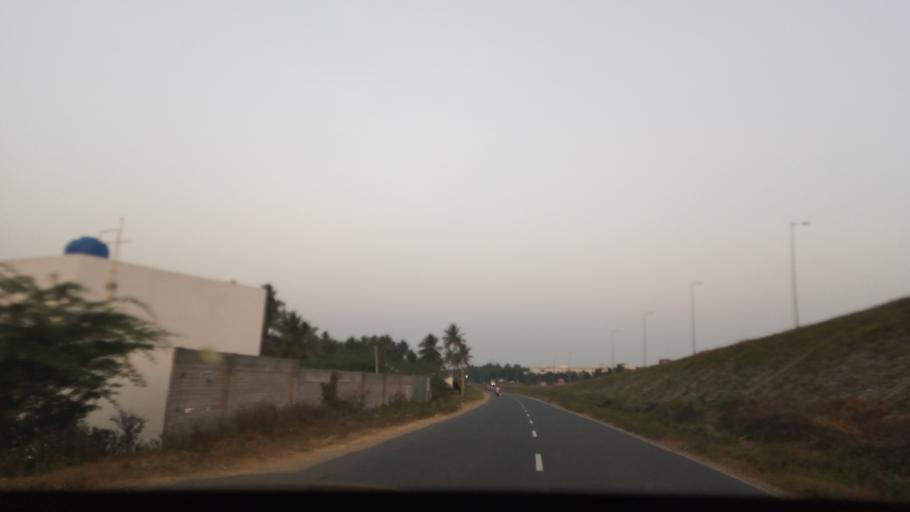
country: IN
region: Tamil Nadu
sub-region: Salem
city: Salem
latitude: 11.6641
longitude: 78.2443
